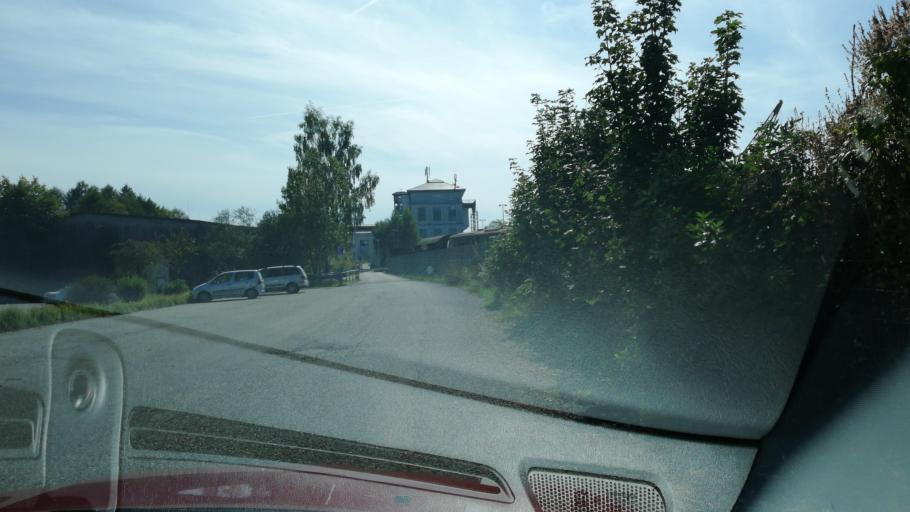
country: AT
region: Upper Austria
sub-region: Politischer Bezirk Vocklabruck
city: Redleiten
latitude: 48.0914
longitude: 13.5621
